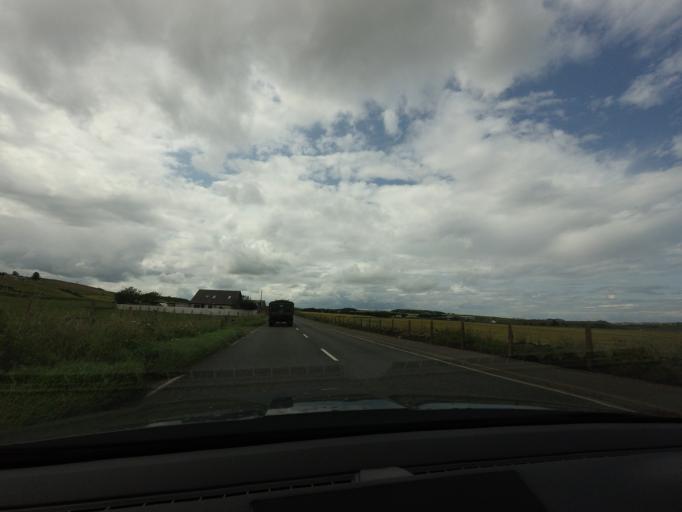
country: GB
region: Scotland
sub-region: Aberdeenshire
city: Banff
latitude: 57.6672
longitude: -2.5496
